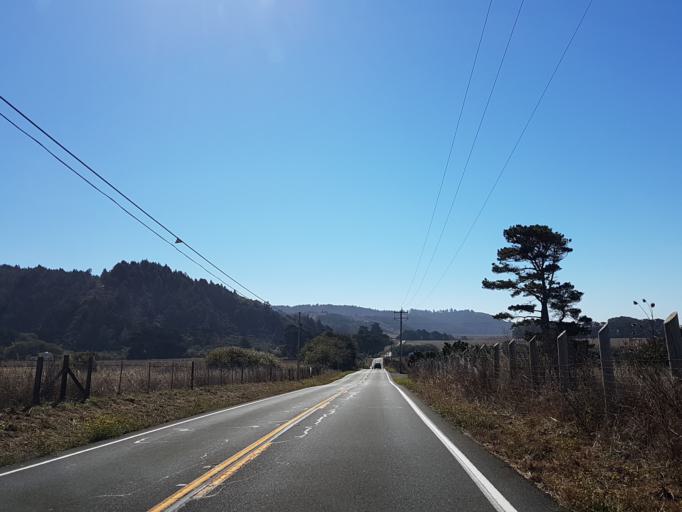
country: US
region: California
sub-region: Mendocino County
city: Boonville
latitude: 39.0643
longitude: -123.6892
